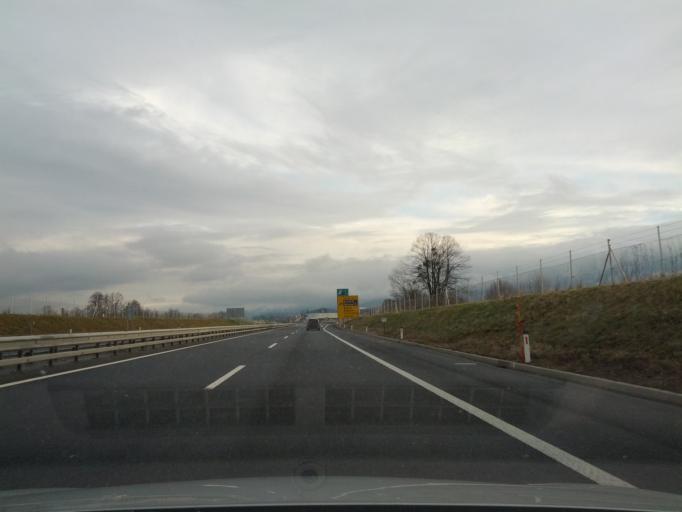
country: SI
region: Radovljica
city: Lesce
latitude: 46.3726
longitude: 14.1572
